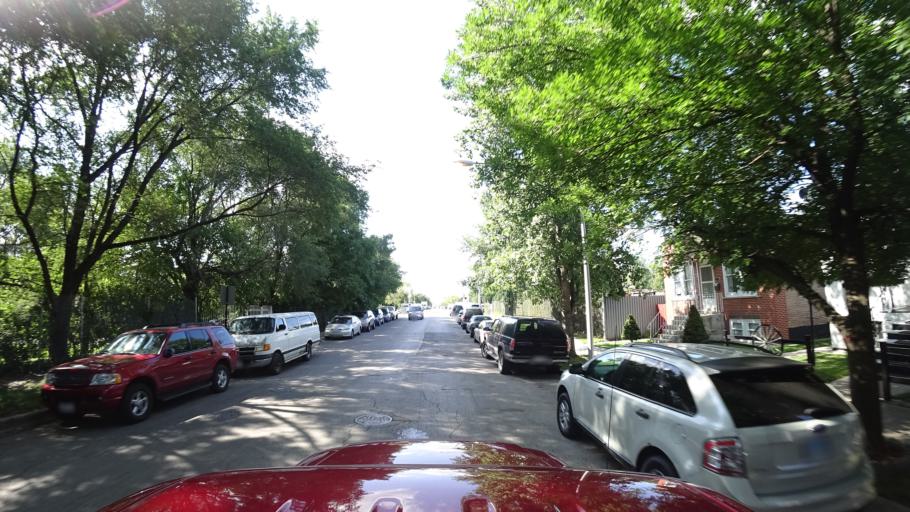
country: US
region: Illinois
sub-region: Cook County
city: Cicero
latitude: 41.8342
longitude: -87.7170
